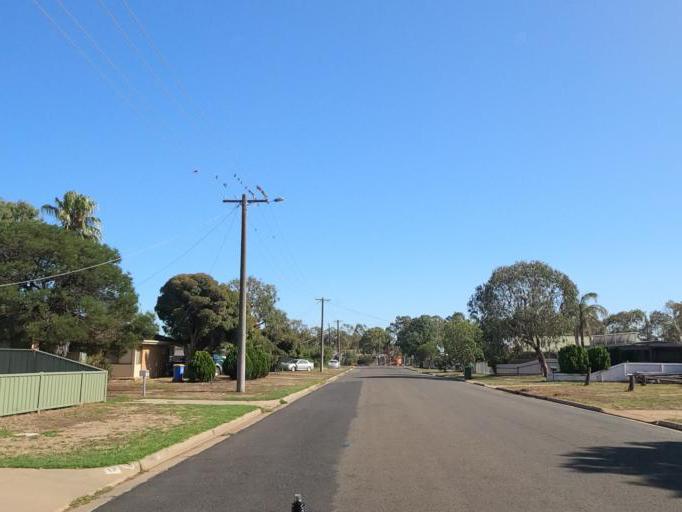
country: AU
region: Victoria
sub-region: Moira
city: Yarrawonga
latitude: -36.0235
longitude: 146.0087
